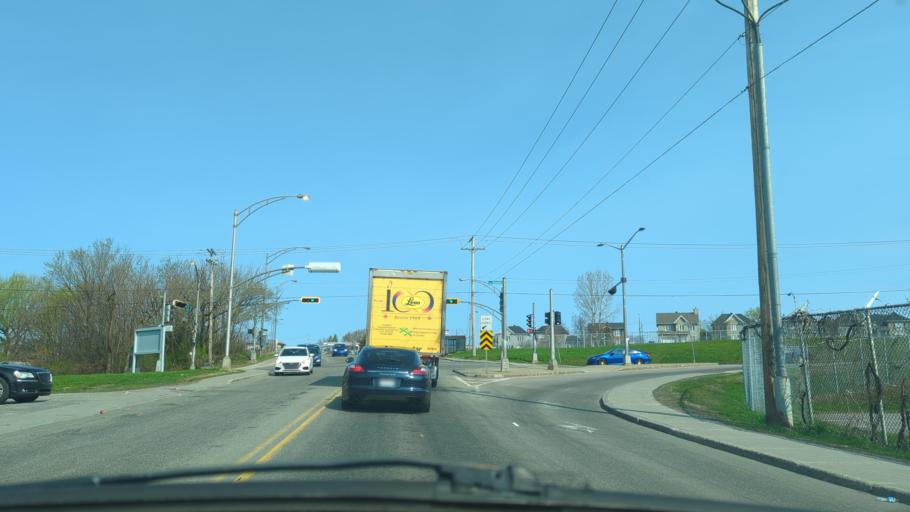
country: CA
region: Quebec
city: Quebec
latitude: 46.8525
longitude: -71.2253
